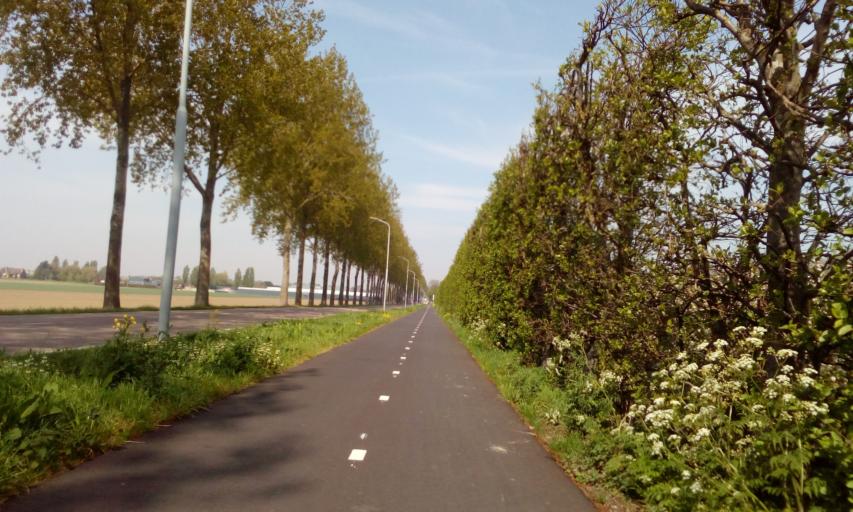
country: NL
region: South Holland
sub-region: Gemeente Lisse
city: Lisse
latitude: 52.2507
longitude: 4.5931
